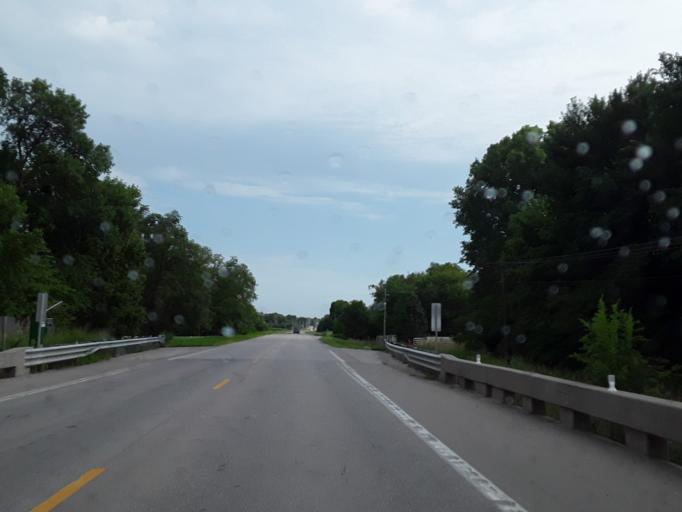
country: US
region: Nebraska
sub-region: Saunders County
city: Ashland
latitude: 41.0538
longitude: -96.3680
